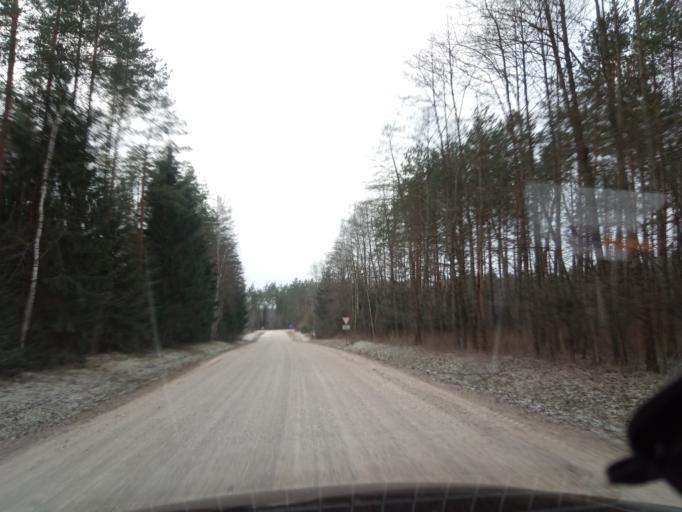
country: LT
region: Alytaus apskritis
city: Varena
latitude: 54.1196
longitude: 24.6390
